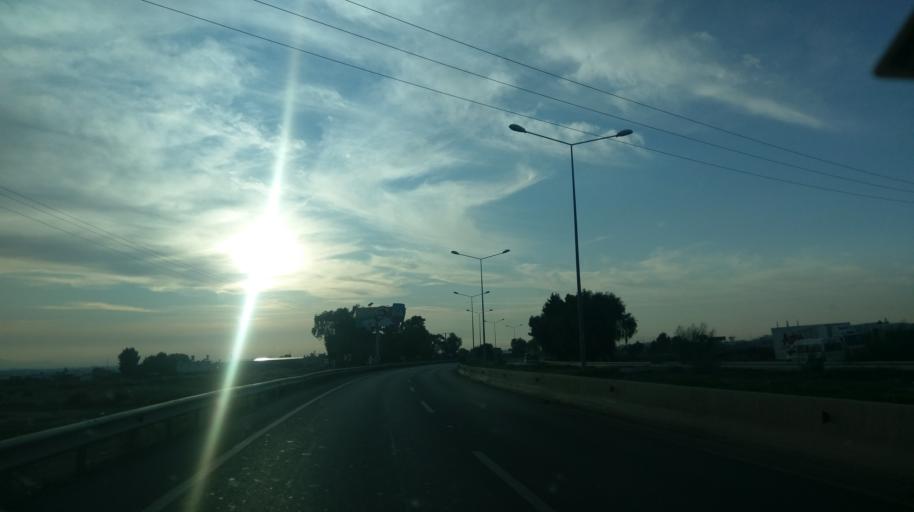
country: CY
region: Lefkosia
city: Nicosia
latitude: 35.2144
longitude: 33.4474
